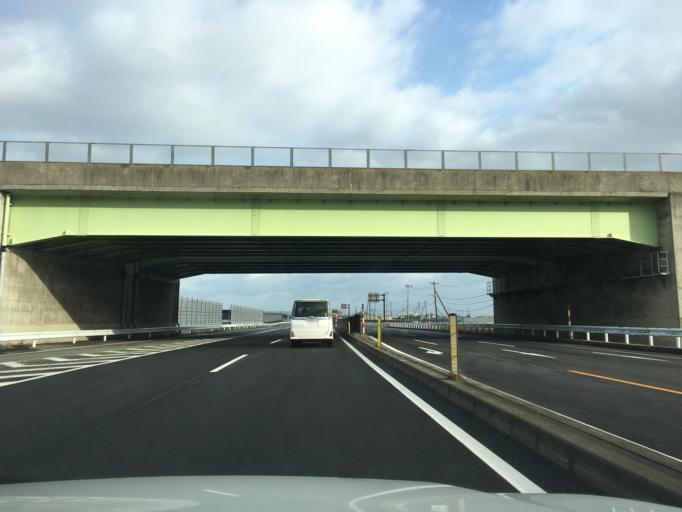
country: JP
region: Yamagata
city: Sakata
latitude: 38.8691
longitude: 139.8419
